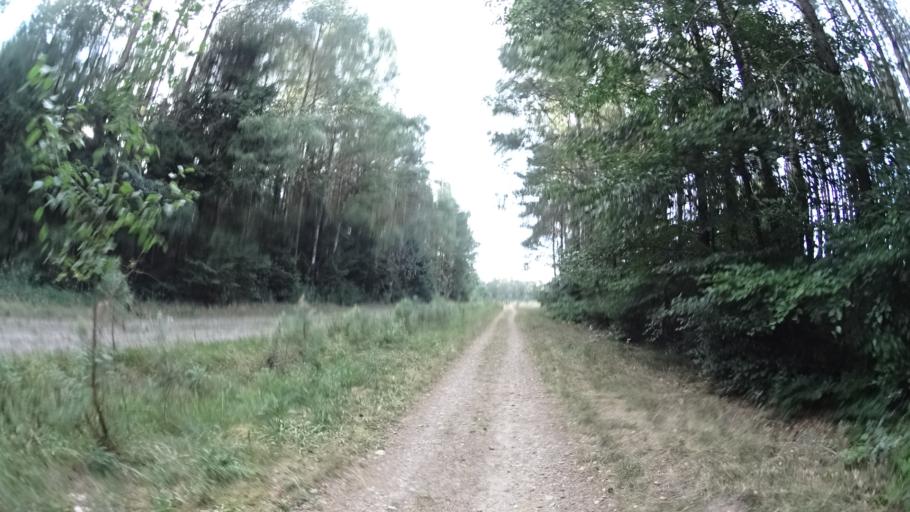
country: DE
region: Lower Saxony
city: Handeloh
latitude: 53.2272
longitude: 9.8738
